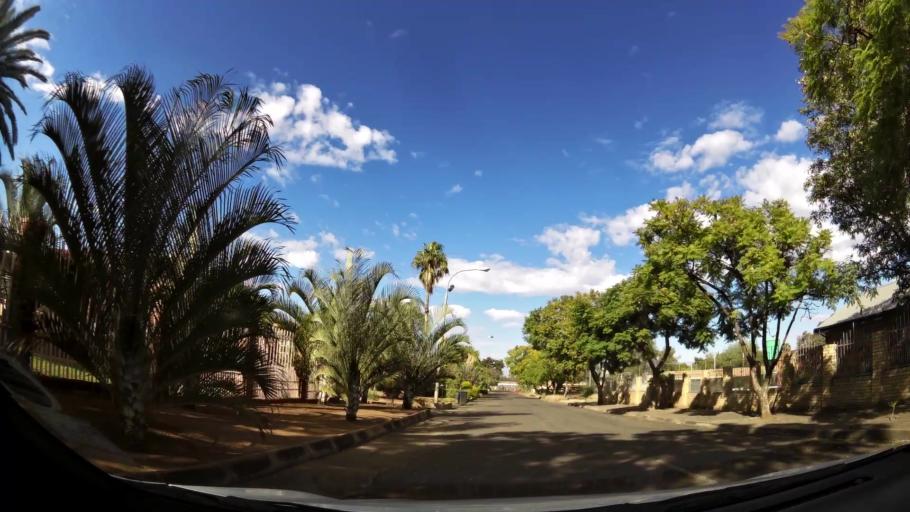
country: ZA
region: Limpopo
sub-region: Waterberg District Municipality
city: Warmbaths
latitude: -24.8791
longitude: 28.2775
